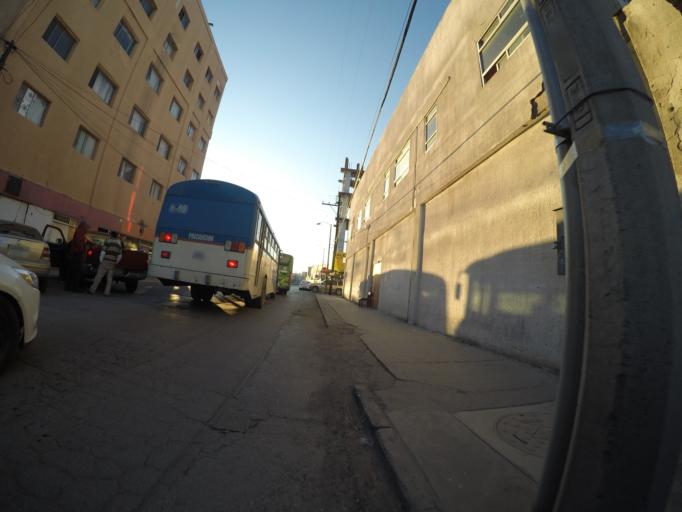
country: MX
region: Chihuahua
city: Ciudad Juarez
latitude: 31.7373
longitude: -106.4810
